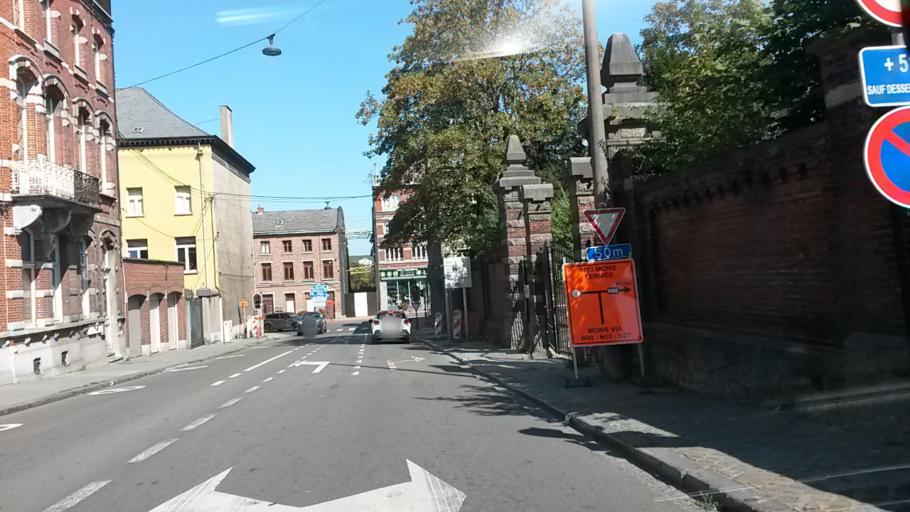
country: BE
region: Wallonia
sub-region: Province du Hainaut
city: Binche
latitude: 50.4113
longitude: 4.1710
